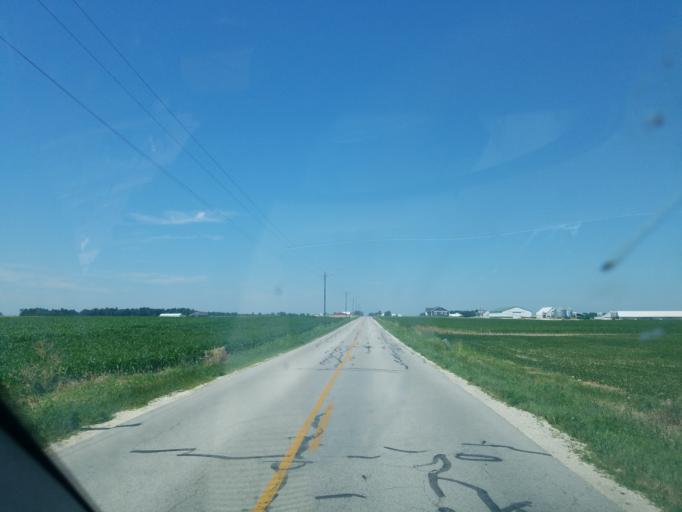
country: US
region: Ohio
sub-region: Mercer County
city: Saint Henry
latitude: 40.4506
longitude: -84.6791
